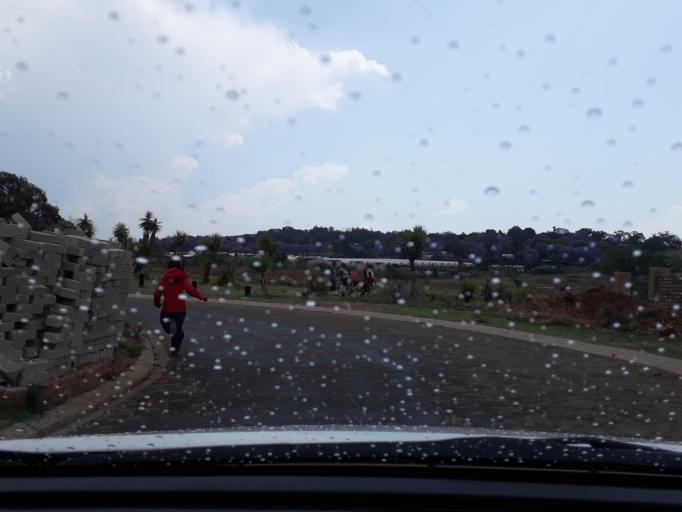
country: ZA
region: Gauteng
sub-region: West Rand District Municipality
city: Muldersdriseloop
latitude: -26.0058
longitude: 27.8523
